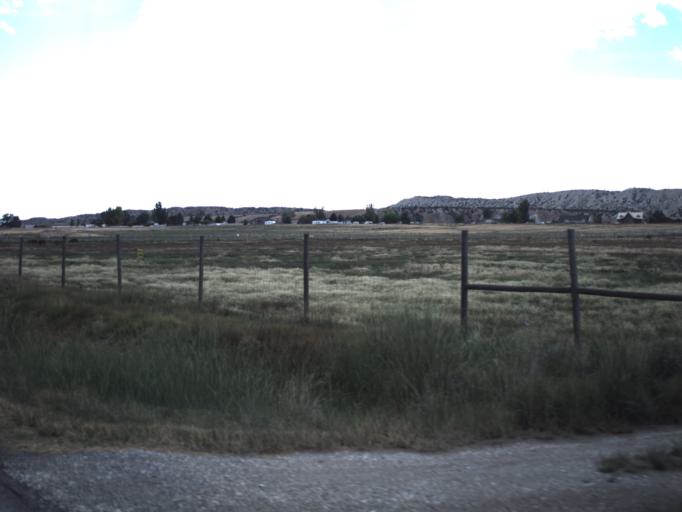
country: US
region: Utah
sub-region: Sanpete County
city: Centerfield
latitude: 39.1351
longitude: -111.7105
